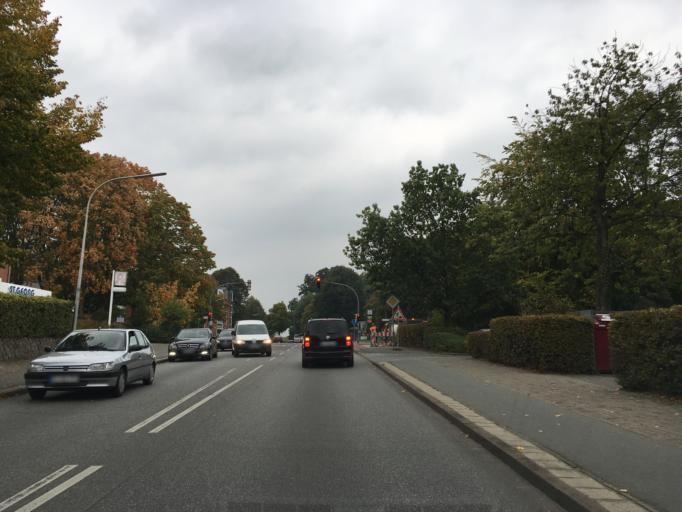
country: DE
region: Schleswig-Holstein
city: Romnitz
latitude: 53.6996
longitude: 10.7501
